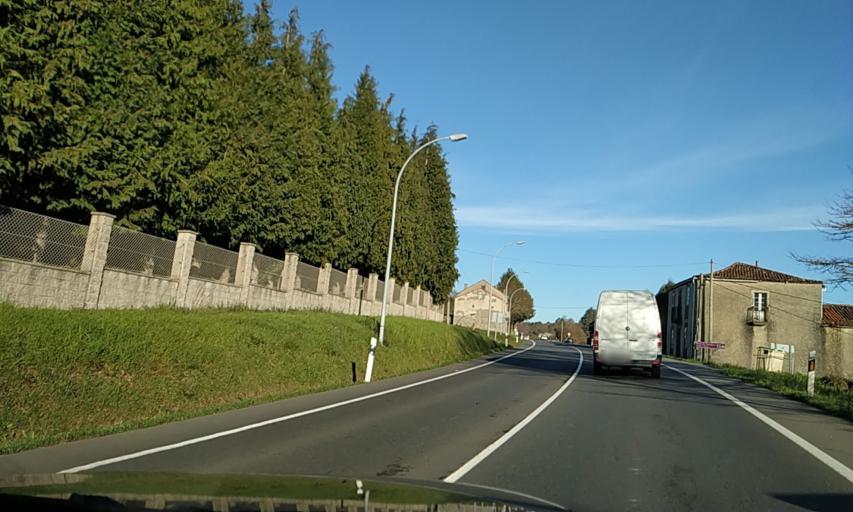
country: ES
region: Galicia
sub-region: Provincia de Pontevedra
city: Lalin
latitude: 42.6815
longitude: -8.1776
